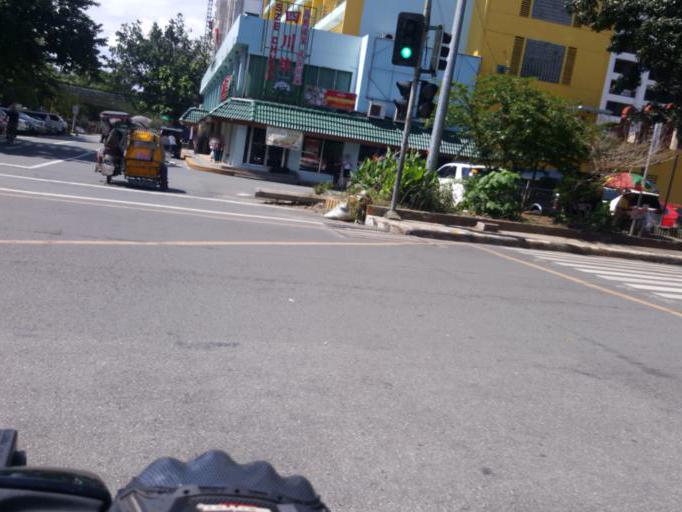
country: PH
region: Metro Manila
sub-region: City of Manila
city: Port Area
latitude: 14.5643
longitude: 120.9854
